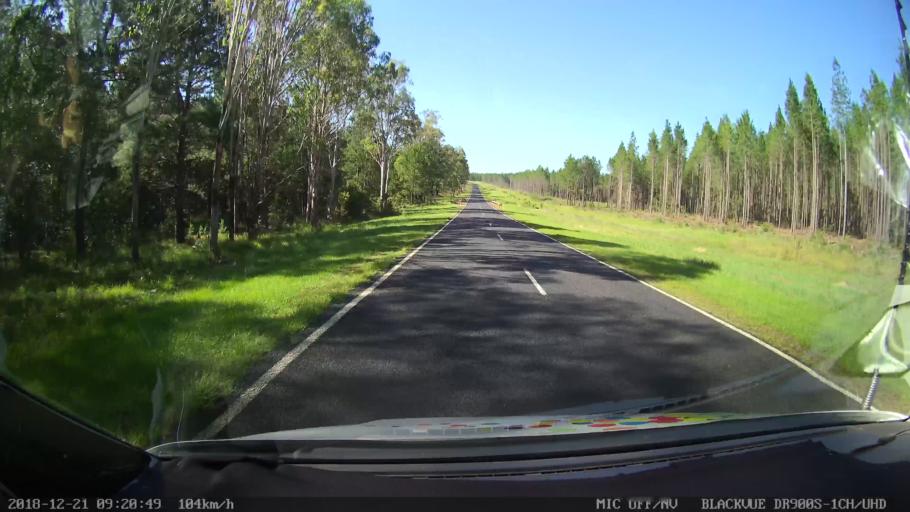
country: AU
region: New South Wales
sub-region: Clarence Valley
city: Maclean
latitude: -29.3200
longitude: 152.9996
